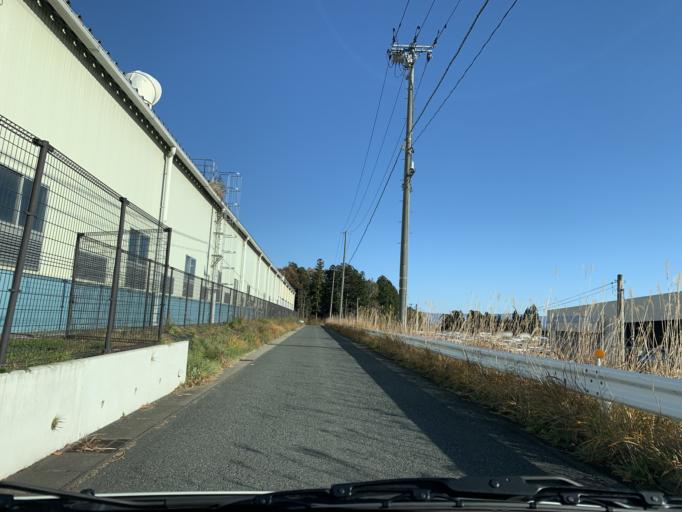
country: JP
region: Iwate
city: Kitakami
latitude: 39.2417
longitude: 141.0931
